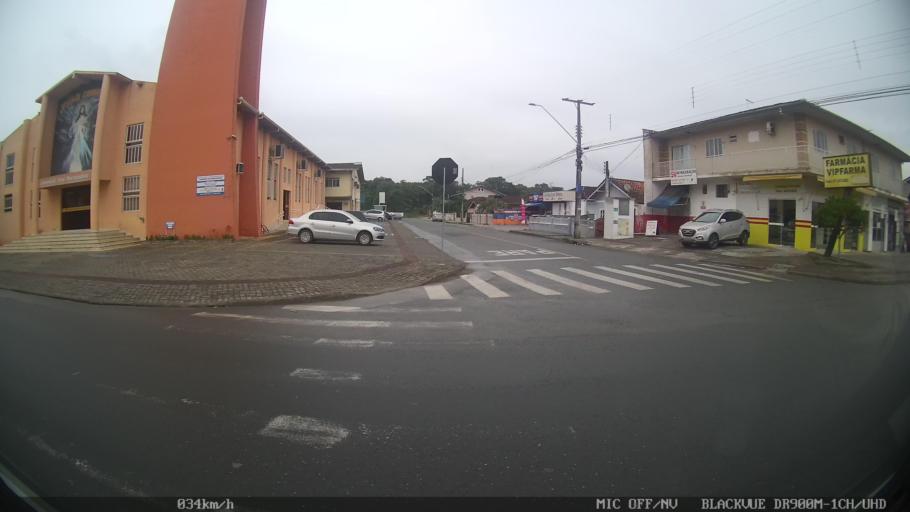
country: BR
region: Santa Catarina
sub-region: Joinville
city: Joinville
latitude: -26.2392
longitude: -48.8075
